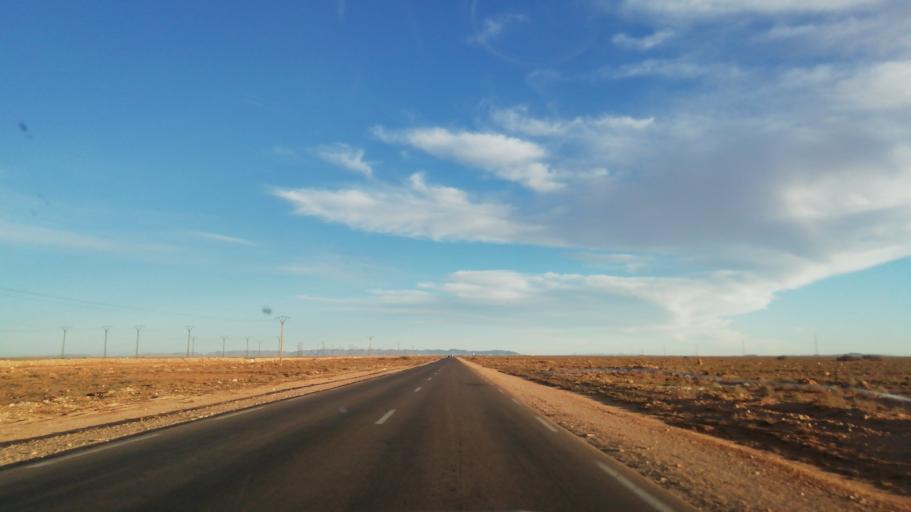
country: DZ
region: Wilaya de Naama
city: Naama
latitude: 33.7420
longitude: -0.7750
